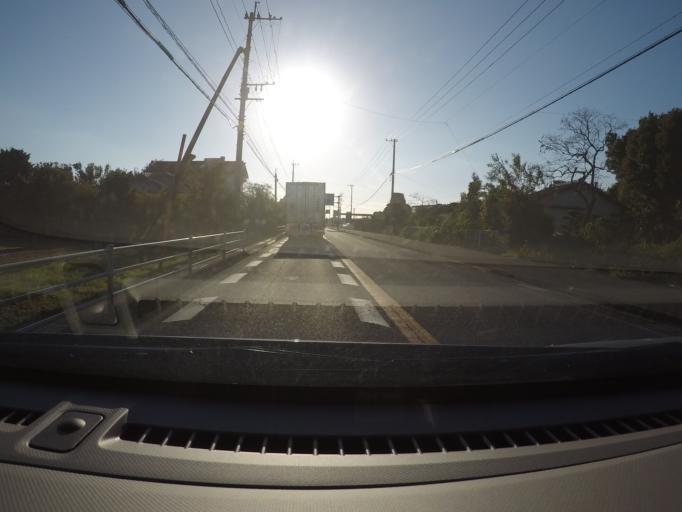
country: JP
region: Kagoshima
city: Izumi
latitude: 32.1042
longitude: 130.3155
